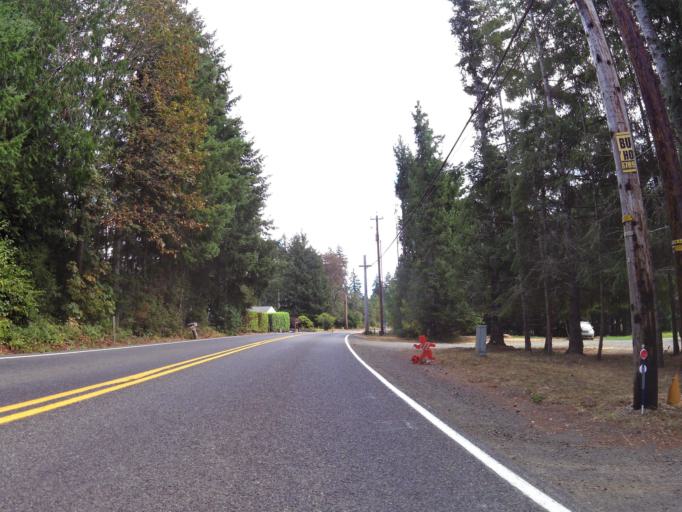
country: US
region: Washington
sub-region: Mason County
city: Shelton
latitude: 47.1810
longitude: -123.0930
